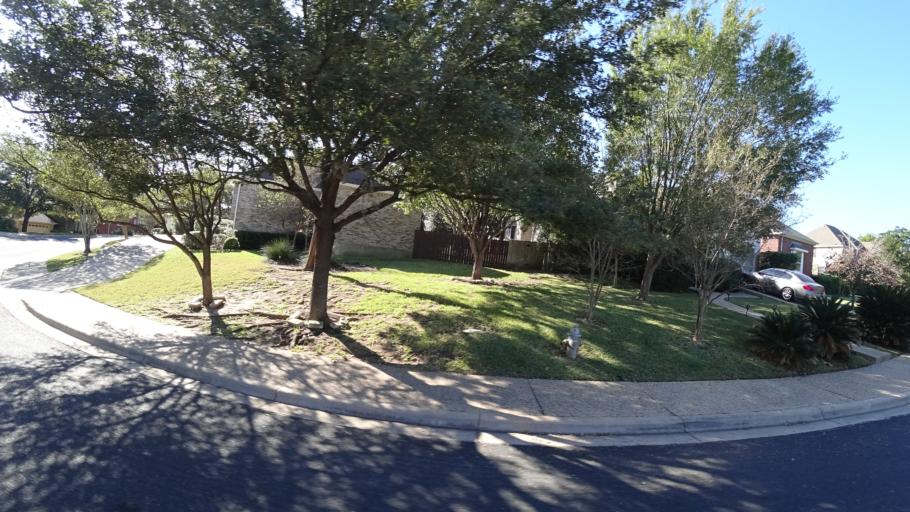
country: US
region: Texas
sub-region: Williamson County
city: Jollyville
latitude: 30.4107
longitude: -97.7583
